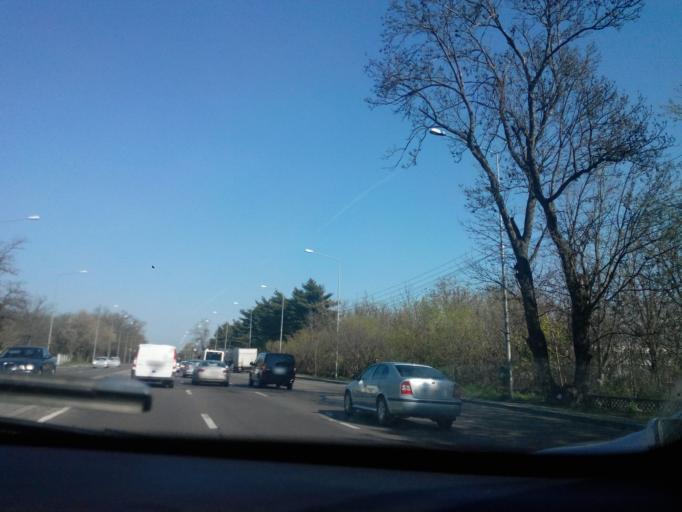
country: RO
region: Ilfov
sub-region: Comuna Otopeni
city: Otopeni
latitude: 44.5194
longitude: 26.0770
